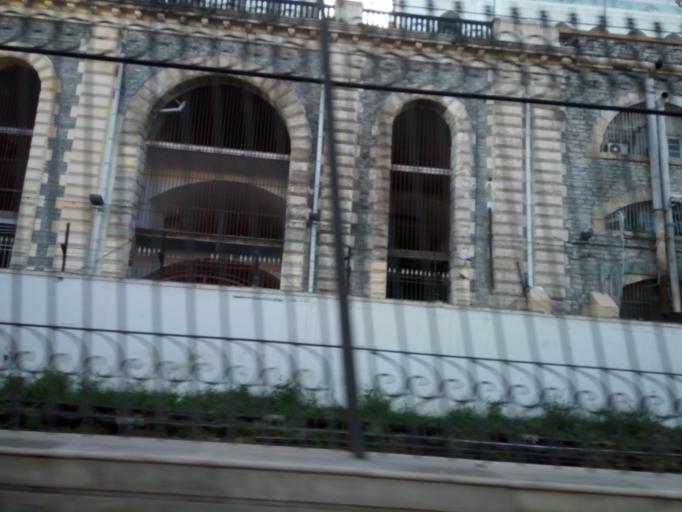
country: DZ
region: Alger
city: Algiers
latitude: 36.7752
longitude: 3.0609
